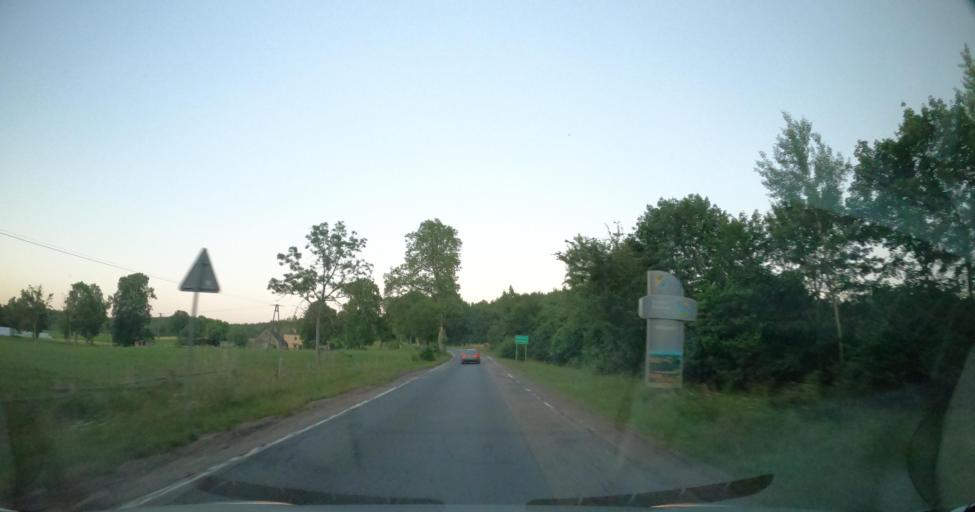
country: PL
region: Pomeranian Voivodeship
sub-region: Powiat wejherowski
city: Luzino
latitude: 54.4663
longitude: 18.0989
